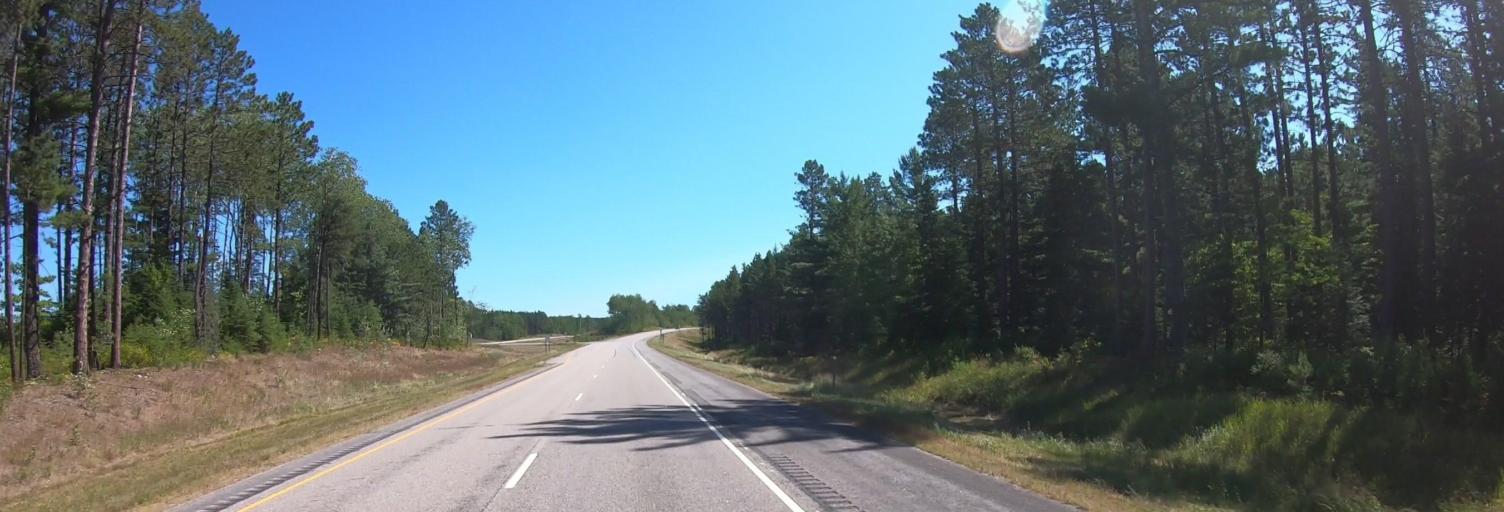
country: US
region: Minnesota
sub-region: Saint Louis County
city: Parkville
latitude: 47.6608
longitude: -92.5966
